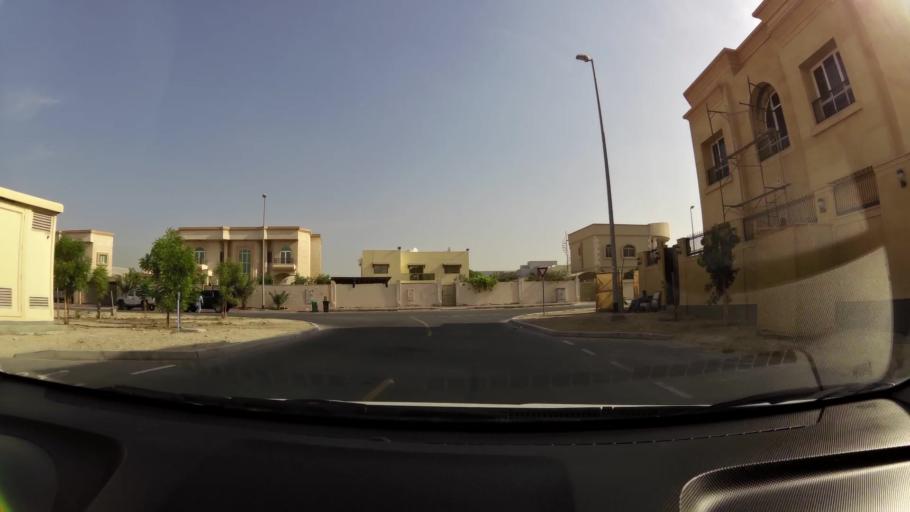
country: AE
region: Ash Shariqah
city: Sharjah
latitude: 25.2423
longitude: 55.4116
